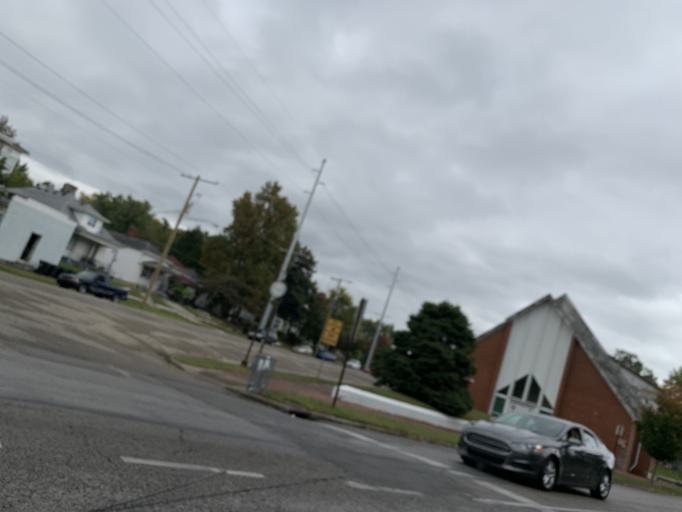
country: US
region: Indiana
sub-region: Floyd County
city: New Albany
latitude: 38.2748
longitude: -85.8006
